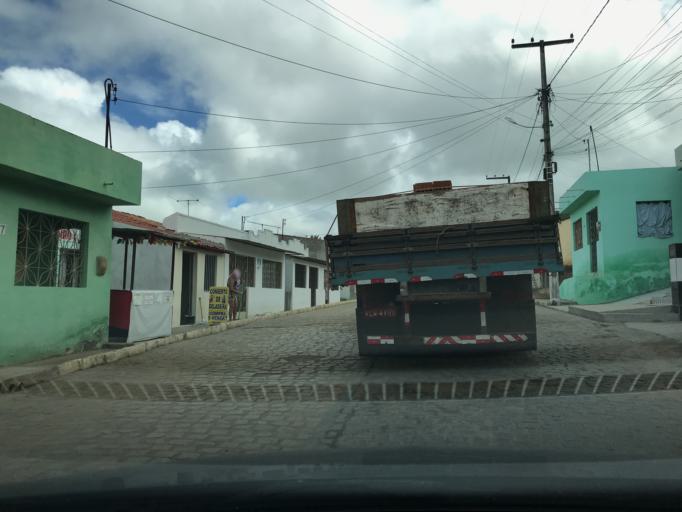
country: BR
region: Pernambuco
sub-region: Bezerros
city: Bezerros
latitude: -8.2292
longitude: -35.7603
